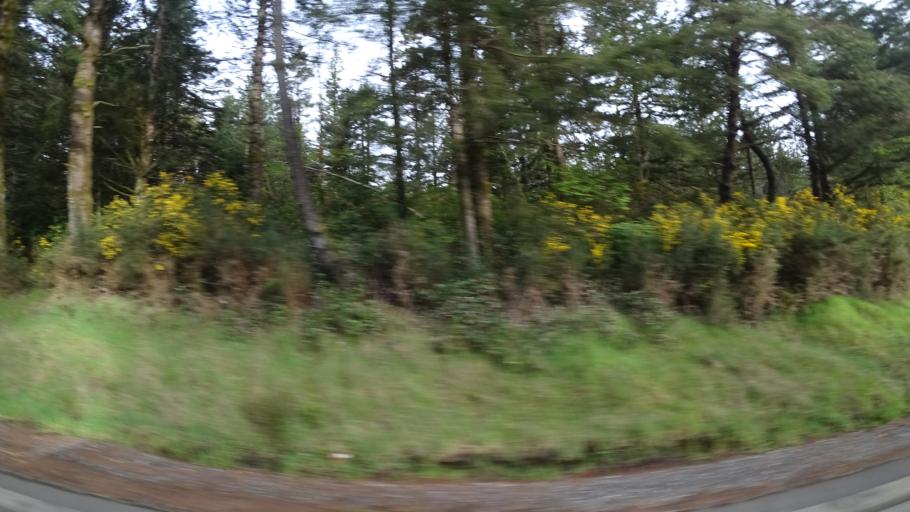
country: US
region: Oregon
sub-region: Coos County
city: Bandon
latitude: 43.1892
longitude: -124.3527
